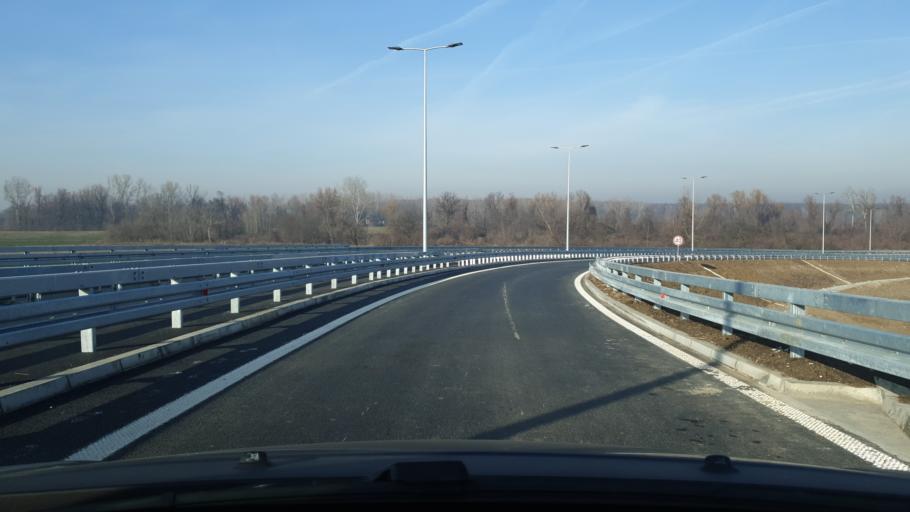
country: RS
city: Baric
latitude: 44.6524
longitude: 20.2308
